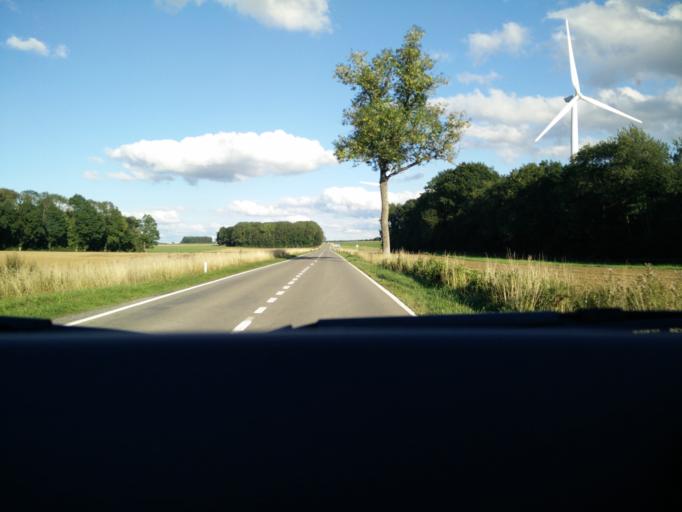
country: BE
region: Wallonia
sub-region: Province du Hainaut
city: Froidchapelle
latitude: 50.2254
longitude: 4.3255
